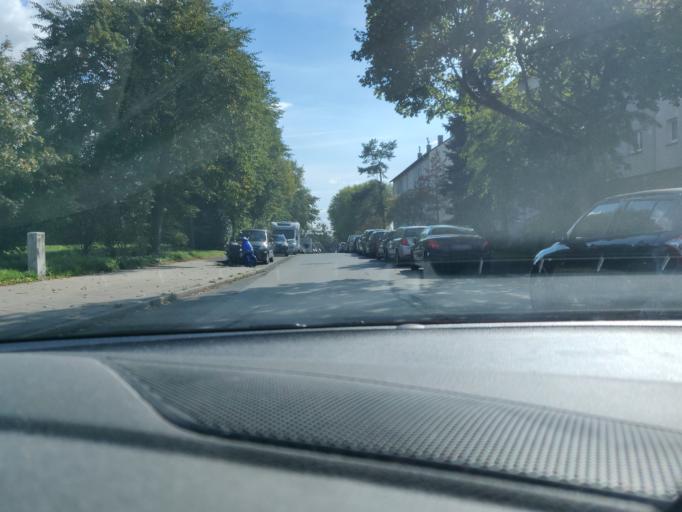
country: DE
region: North Rhine-Westphalia
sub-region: Regierungsbezirk Dusseldorf
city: Velbert
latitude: 51.3317
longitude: 7.0236
